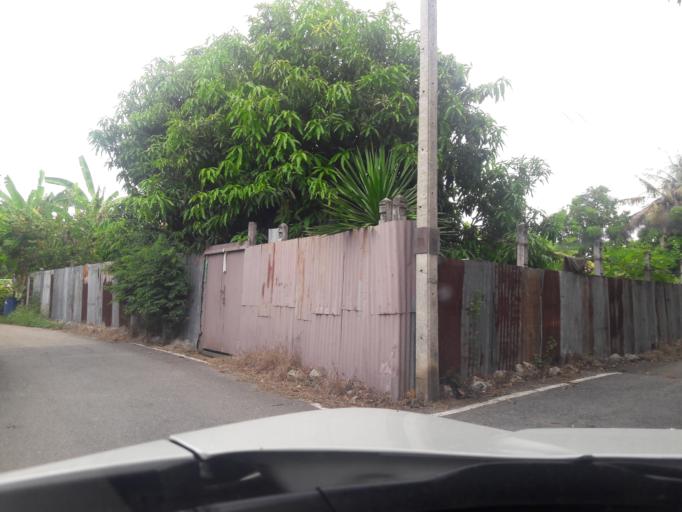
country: TH
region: Lop Buri
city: Ban Mi
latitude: 15.0463
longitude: 100.5467
